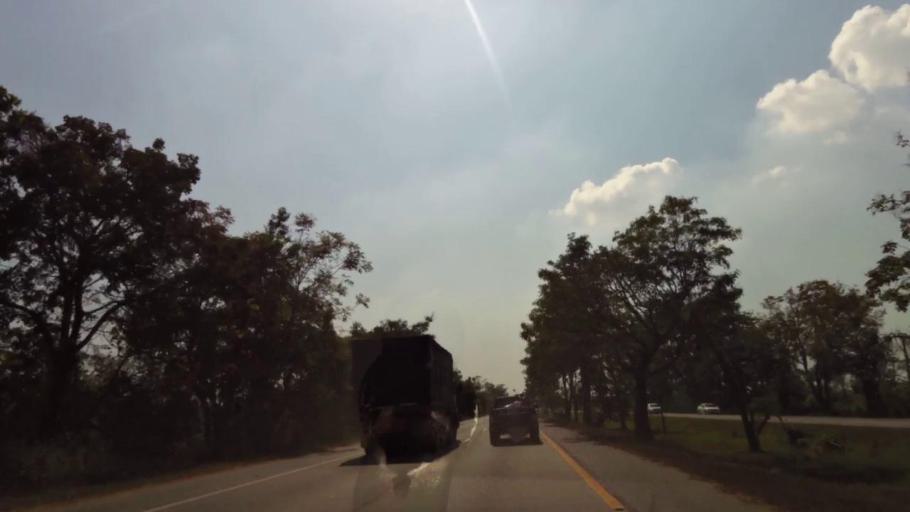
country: TH
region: Phichit
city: Wachira Barami
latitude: 16.5458
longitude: 100.1458
